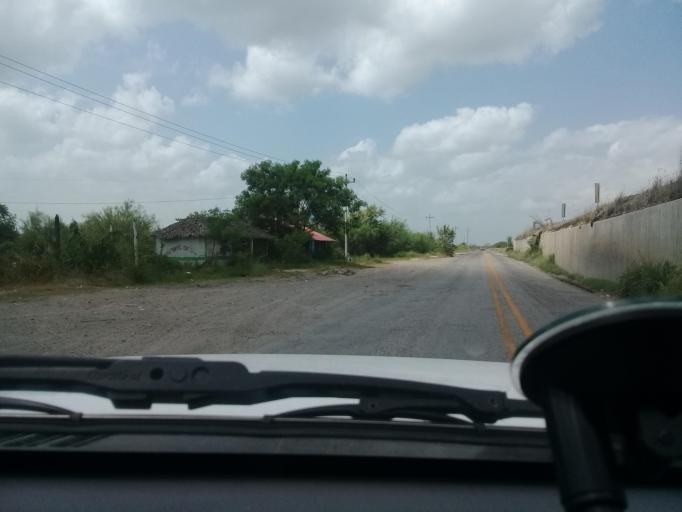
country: MX
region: Veracruz
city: Moralillo
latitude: 22.1825
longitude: -98.0192
